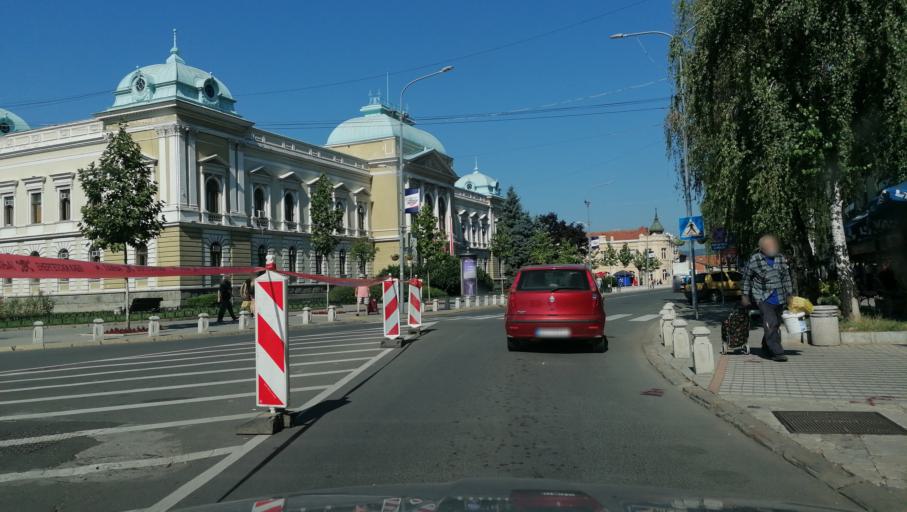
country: RS
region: Central Serbia
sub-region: Rasinski Okrug
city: Krusevac
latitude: 43.5832
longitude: 21.3259
